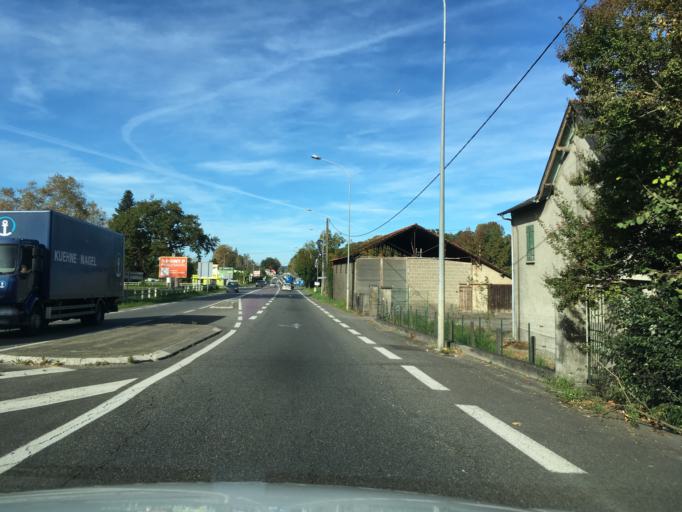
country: FR
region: Aquitaine
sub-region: Departement des Pyrenees-Atlantiques
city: Lons
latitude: 43.3432
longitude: -0.3798
